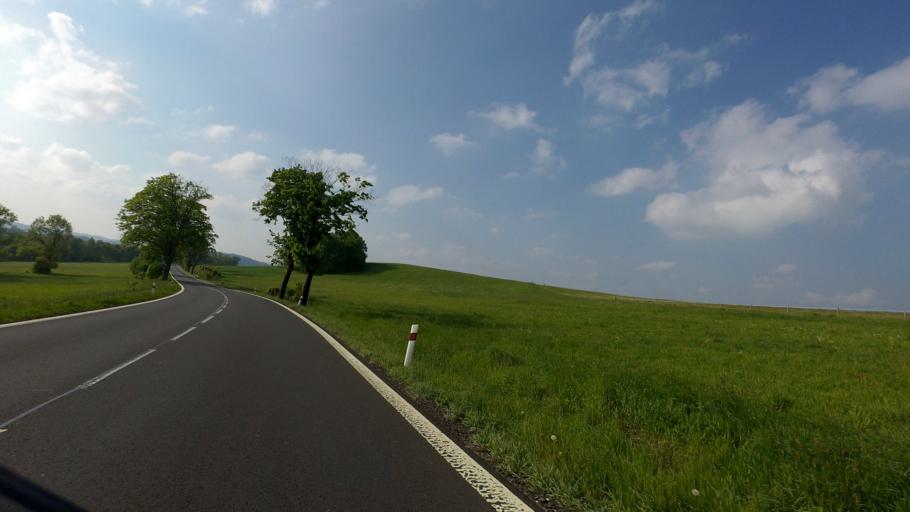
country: CZ
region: Ustecky
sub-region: Okres Decin
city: Sluknov
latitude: 50.9947
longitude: 14.4806
